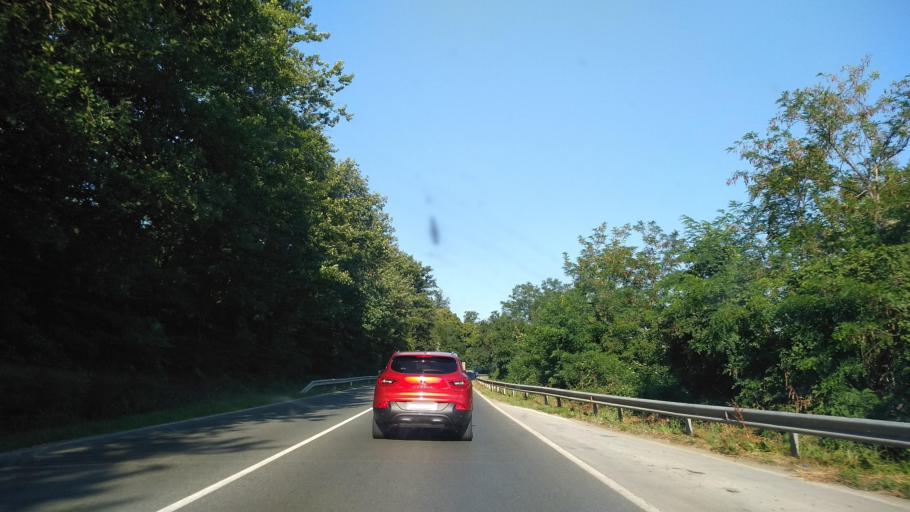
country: BG
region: Lovech
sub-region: Obshtina Teteven
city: Teteven
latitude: 43.0549
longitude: 24.2515
